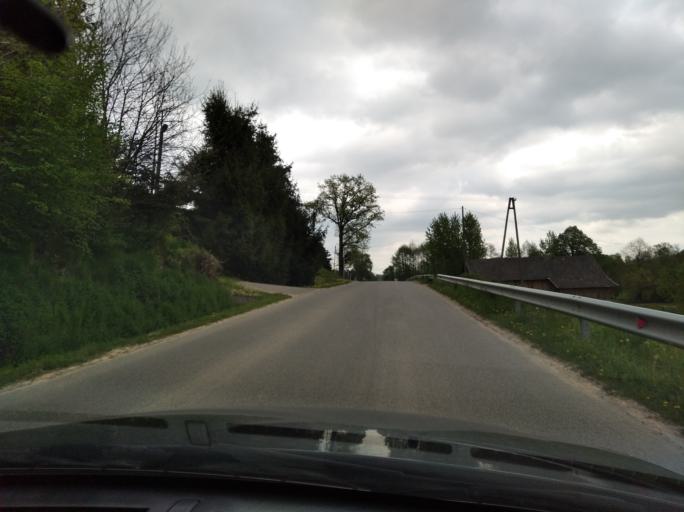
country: PL
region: Subcarpathian Voivodeship
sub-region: Powiat debicki
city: Leki Gorne
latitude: 49.9748
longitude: 21.1923
